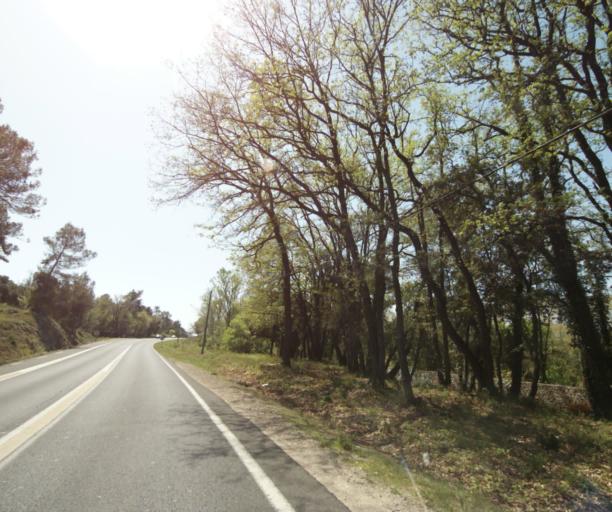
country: FR
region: Languedoc-Roussillon
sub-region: Departement de l'Herault
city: Montferrier-sur-Lez
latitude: 43.6657
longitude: 3.8662
